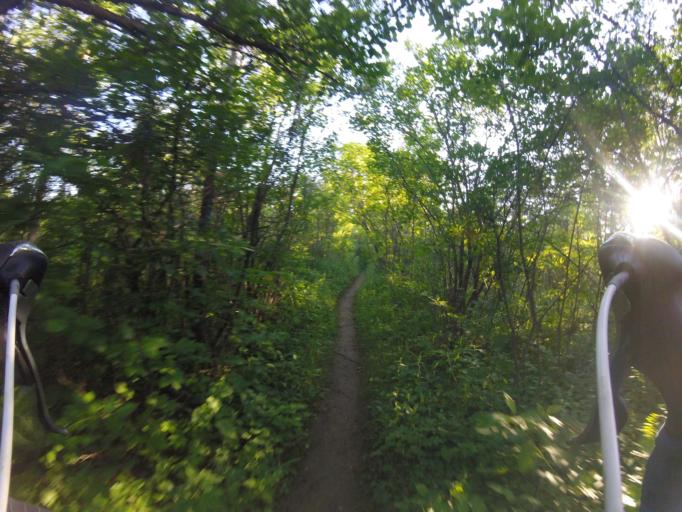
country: CA
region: Ontario
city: Bells Corners
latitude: 45.3556
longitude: -75.8602
